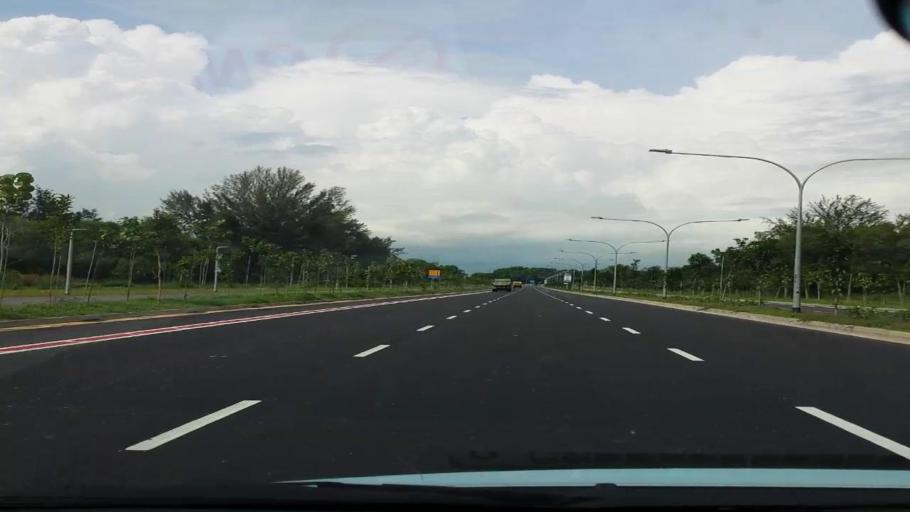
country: SG
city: Singapore
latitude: 1.3232
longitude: 104.0179
